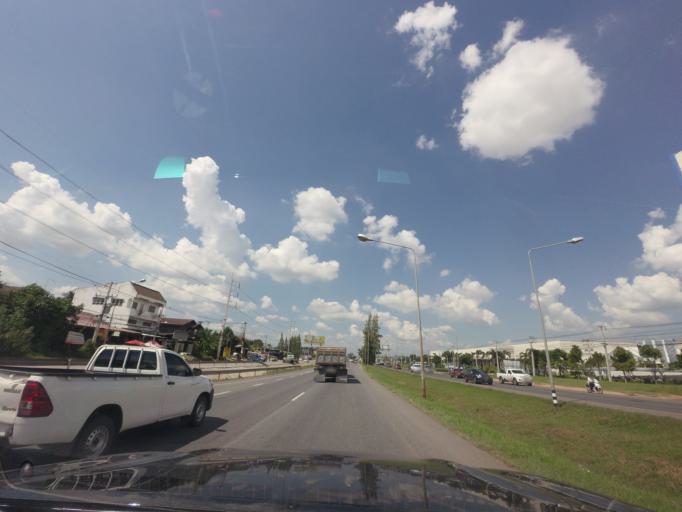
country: TH
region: Nakhon Ratchasima
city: Nakhon Ratchasima
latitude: 14.9769
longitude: 102.0520
